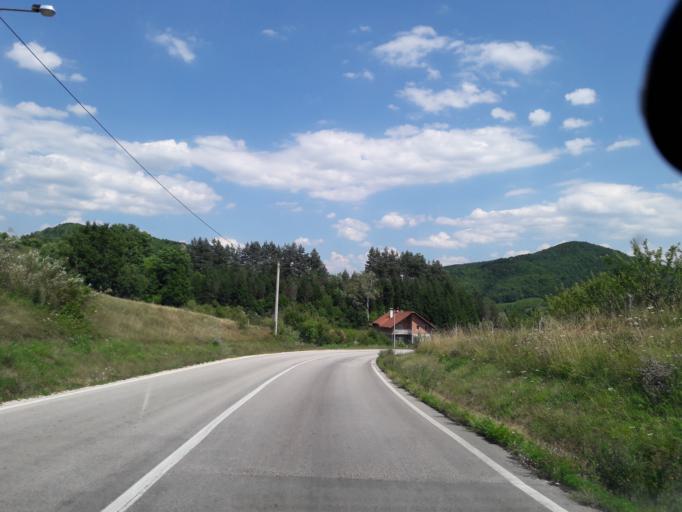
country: BA
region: Republika Srpska
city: Mrkonjic Grad
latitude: 44.4214
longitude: 17.1091
